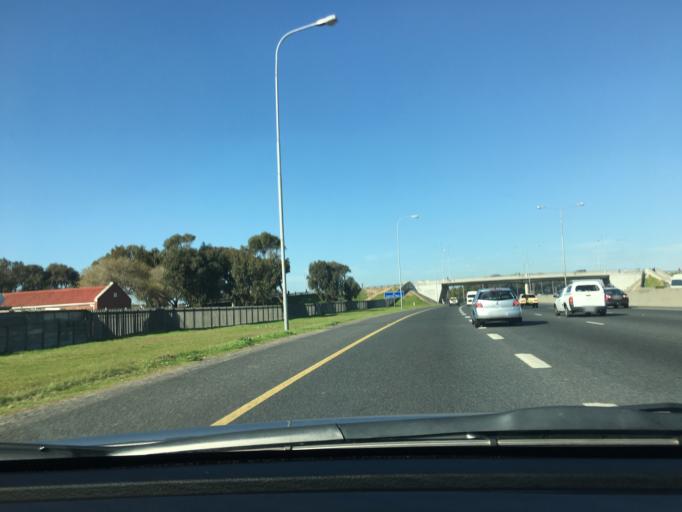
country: ZA
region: Western Cape
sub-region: City of Cape Town
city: Lansdowne
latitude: -33.9630
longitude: 18.5666
